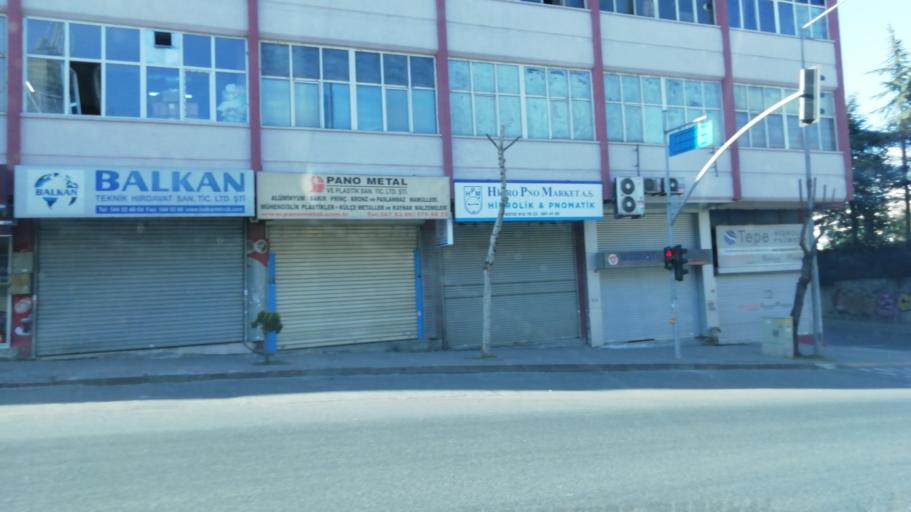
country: TR
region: Istanbul
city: Istanbul
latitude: 41.0325
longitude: 28.9189
